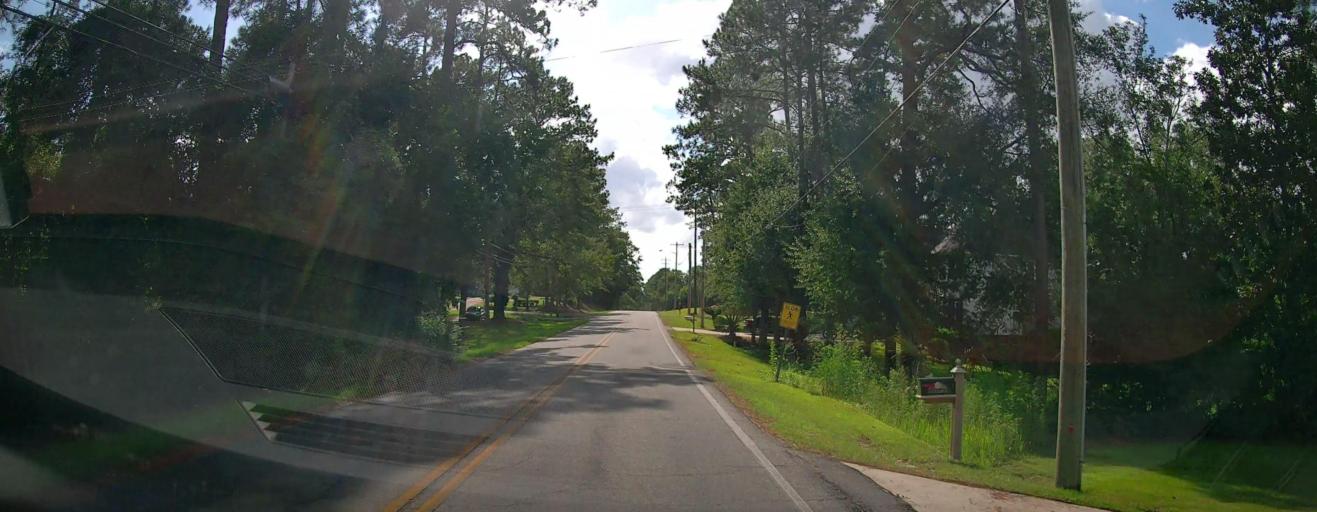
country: US
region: Georgia
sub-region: Coffee County
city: Douglas
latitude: 31.5167
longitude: -82.8372
